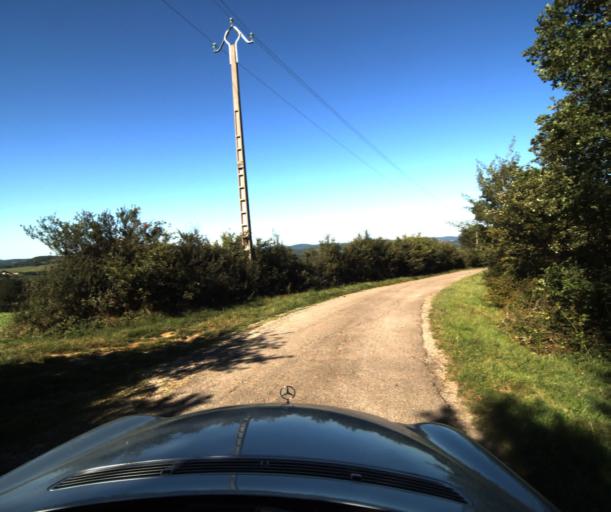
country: FR
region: Midi-Pyrenees
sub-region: Departement de l'Ariege
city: Lavelanet
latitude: 42.9731
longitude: 1.8893
